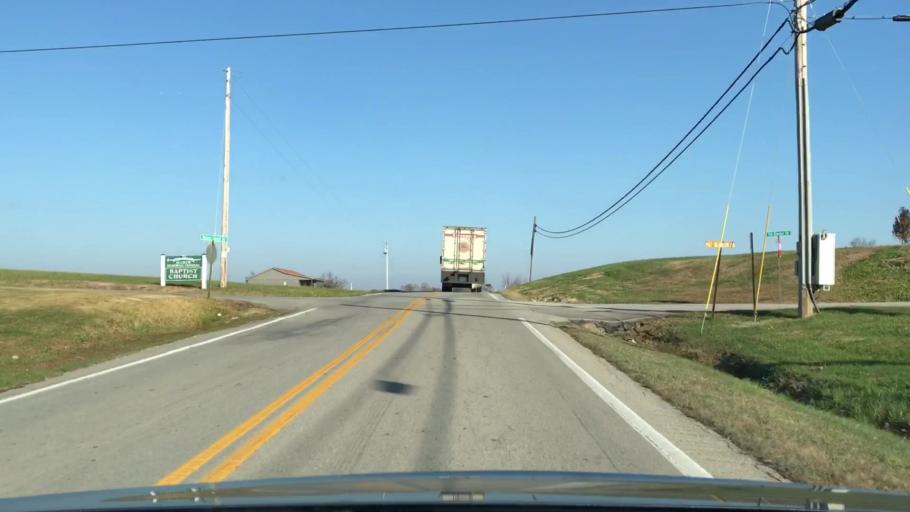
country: US
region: Kentucky
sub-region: Grayson County
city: Leitchfield
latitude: 37.3615
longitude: -86.2417
